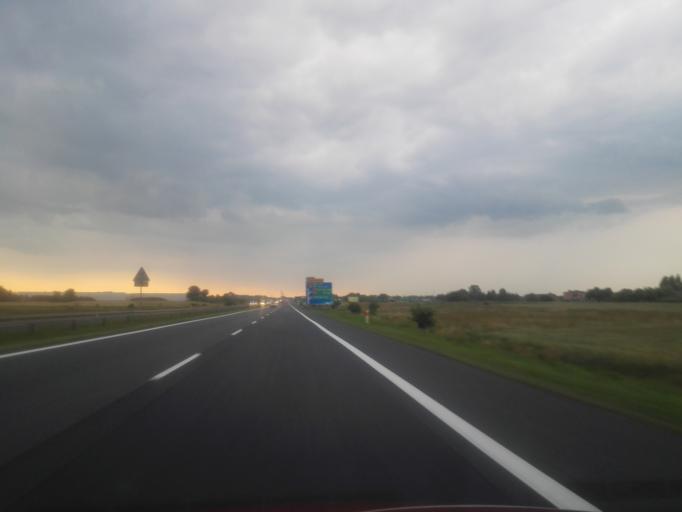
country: PL
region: Lodz Voivodeship
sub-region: Piotrkow Trybunalski
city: Piotrkow Trybunalski
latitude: 51.4000
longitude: 19.6317
